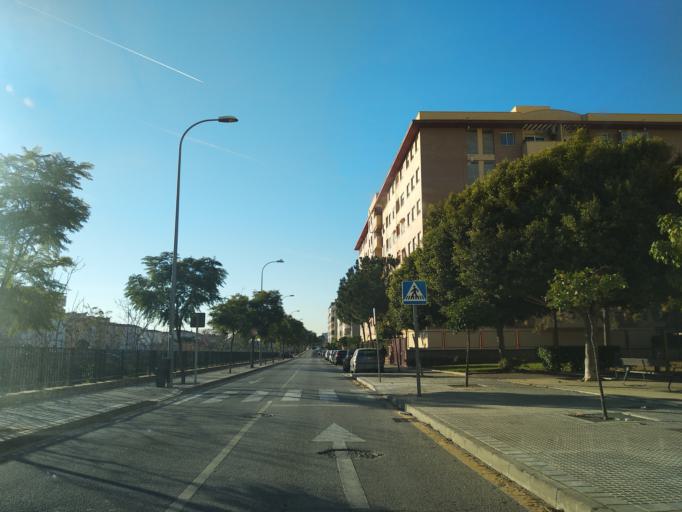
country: ES
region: Andalusia
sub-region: Provincia de Malaga
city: Malaga
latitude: 36.7465
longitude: -4.4252
